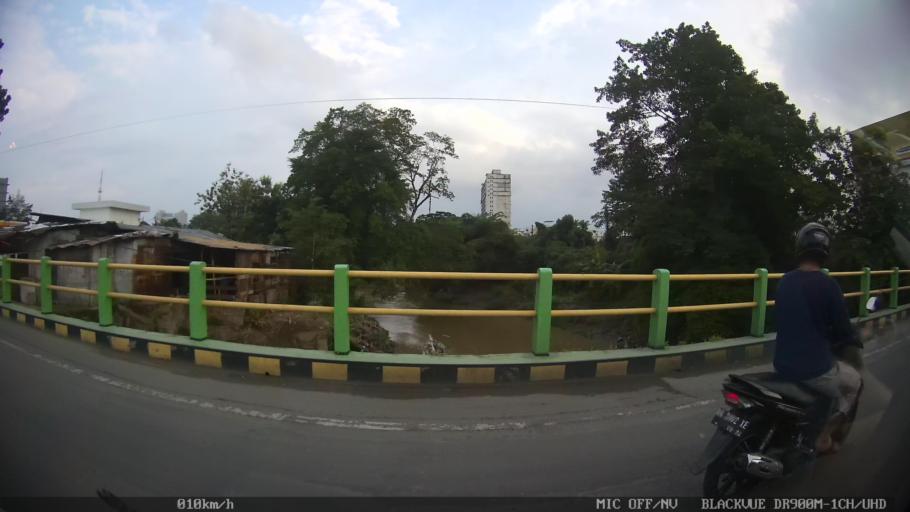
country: ID
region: North Sumatra
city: Medan
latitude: 3.6067
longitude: 98.6713
